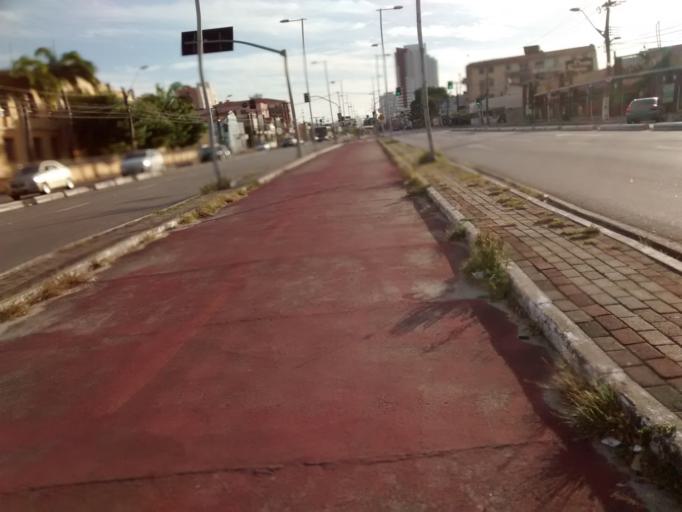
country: BR
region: Ceara
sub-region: Fortaleza
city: Fortaleza
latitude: -3.7327
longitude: -38.5503
